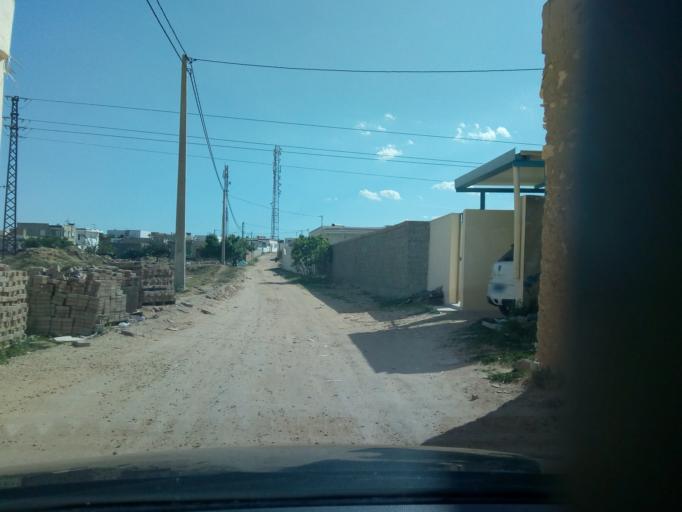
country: TN
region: Safaqis
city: Sfax
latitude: 34.7291
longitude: 10.6082
